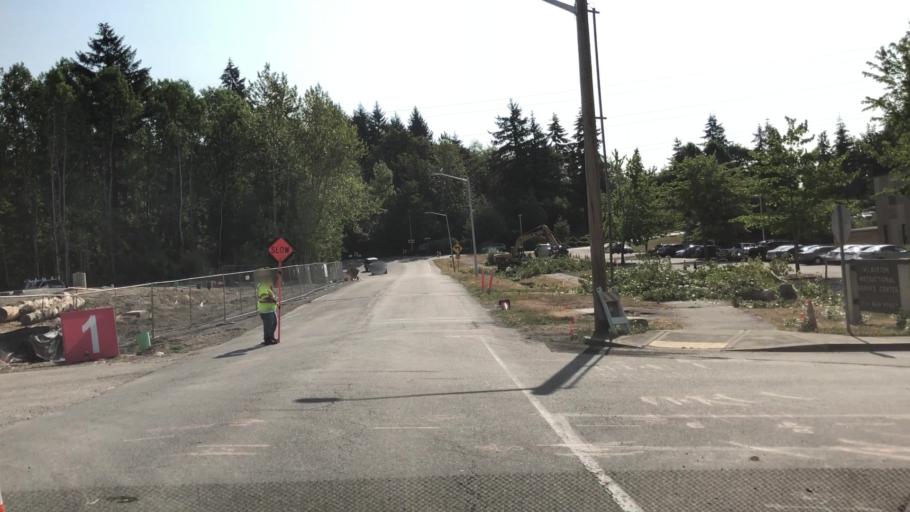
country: US
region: Washington
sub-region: King County
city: Bellevue
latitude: 47.6100
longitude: -122.1769
